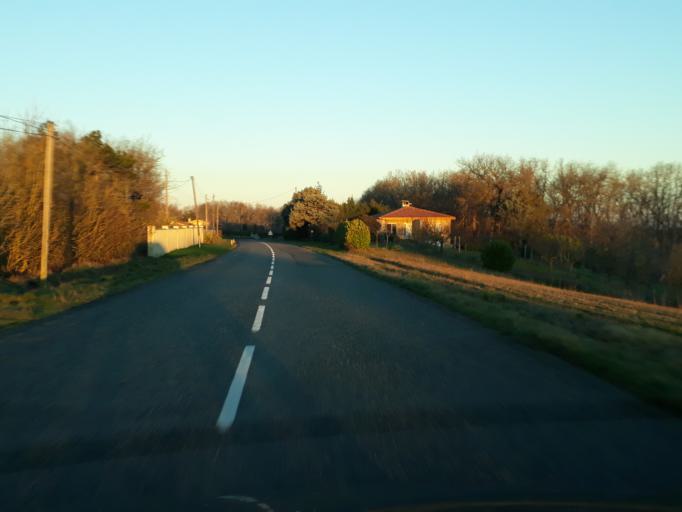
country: FR
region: Midi-Pyrenees
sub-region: Departement du Gers
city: Pavie
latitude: 43.6063
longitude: 0.6883
